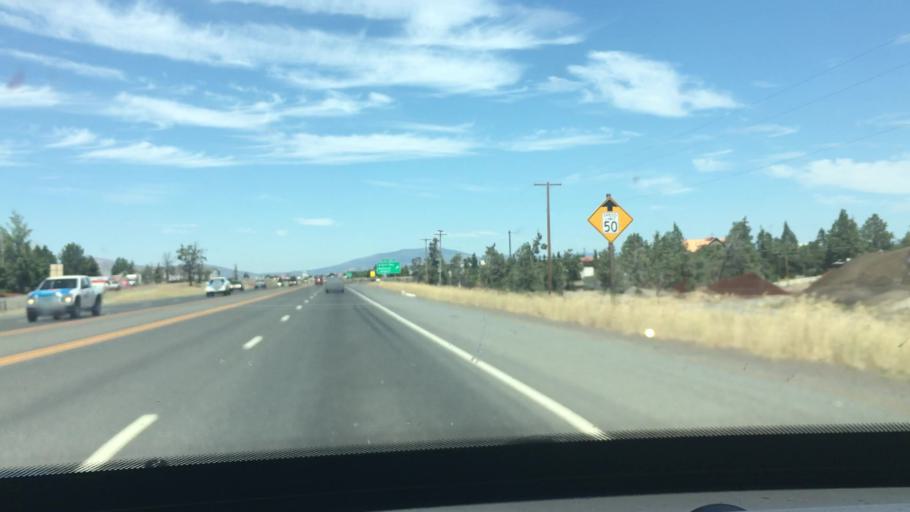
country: US
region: Oregon
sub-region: Deschutes County
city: Redmond
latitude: 44.2375
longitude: -121.1980
